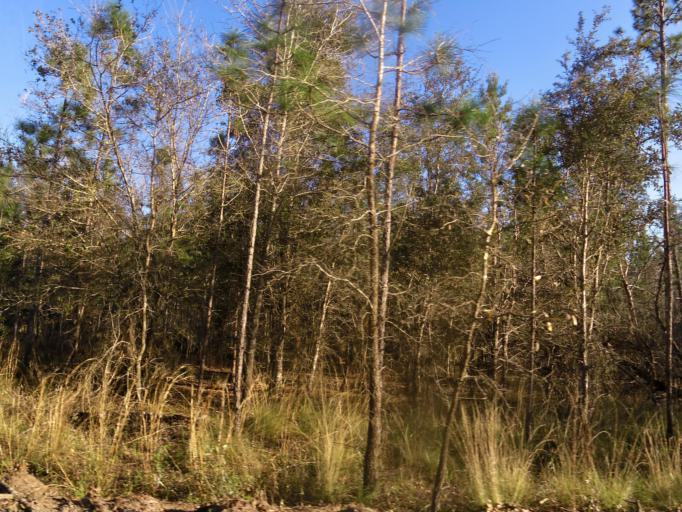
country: US
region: Florida
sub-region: Clay County
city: Middleburg
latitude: 30.1499
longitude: -81.8878
